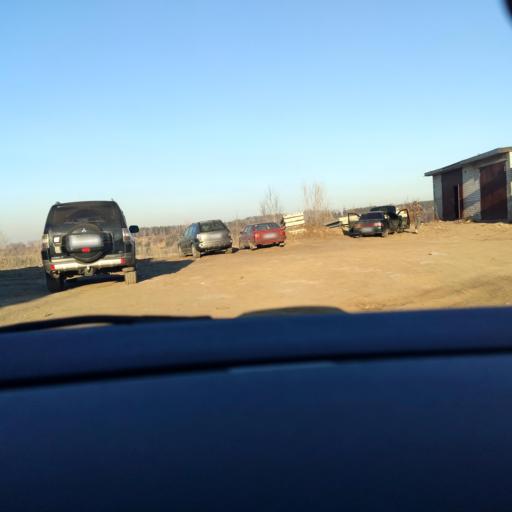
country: RU
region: Voronezj
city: Pridonskoy
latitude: 51.6901
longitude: 39.0784
